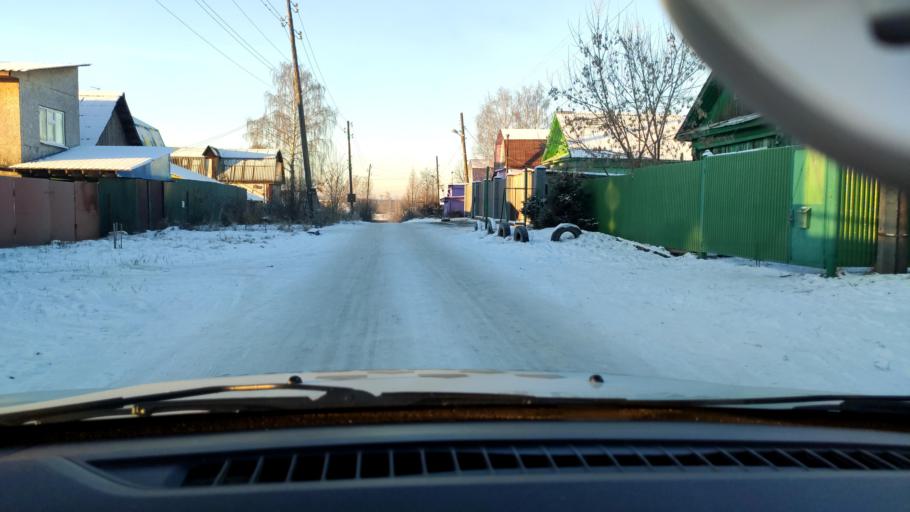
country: RU
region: Perm
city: Kondratovo
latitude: 58.0479
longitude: 56.0375
